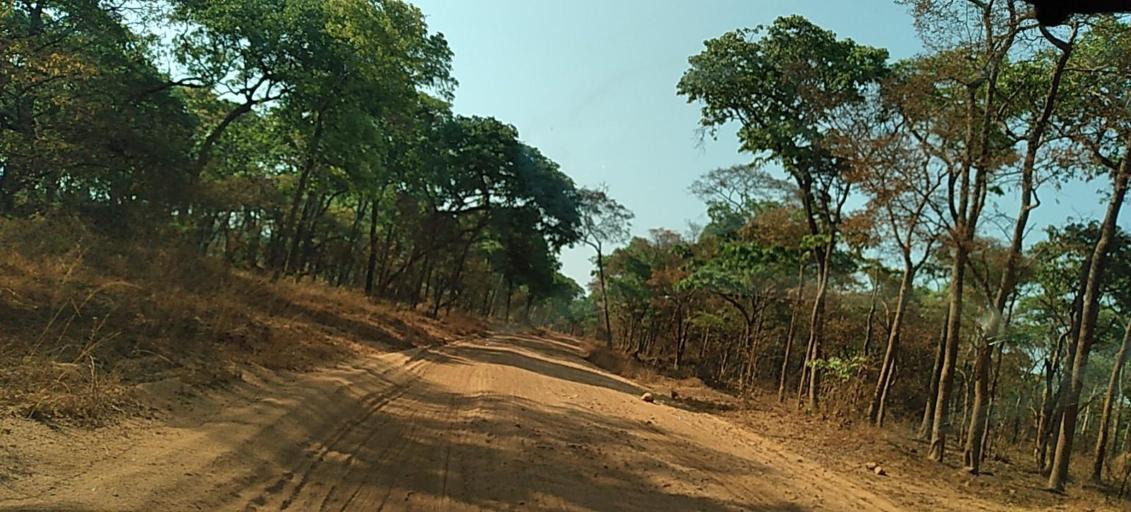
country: ZM
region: North-Western
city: Kasempa
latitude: -13.6667
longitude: 26.0130
